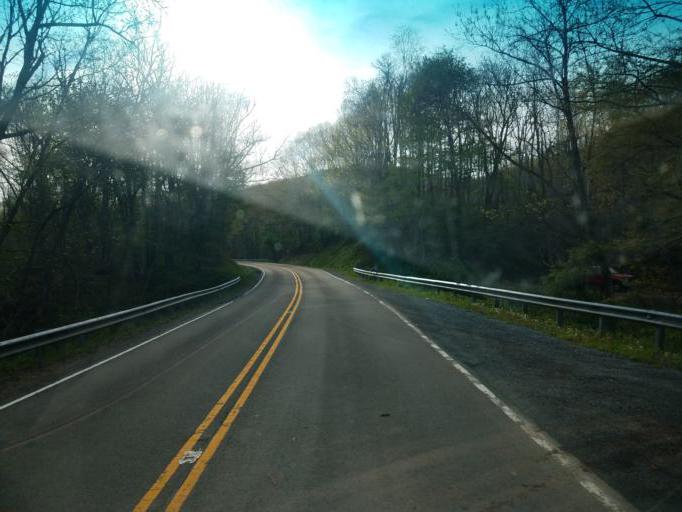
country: US
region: Virginia
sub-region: Smyth County
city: Atkins
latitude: 36.8175
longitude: -81.4376
